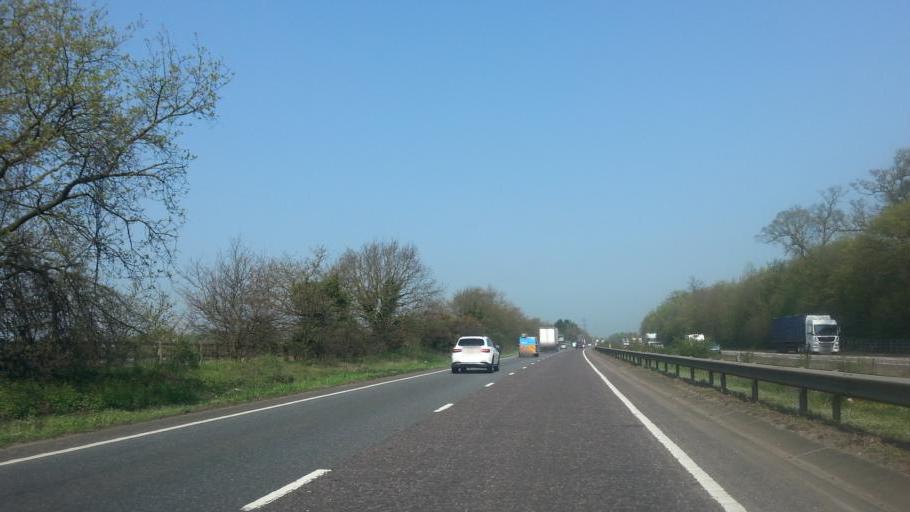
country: GB
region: England
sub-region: Suffolk
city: Needham Market
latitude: 52.1378
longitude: 1.0866
